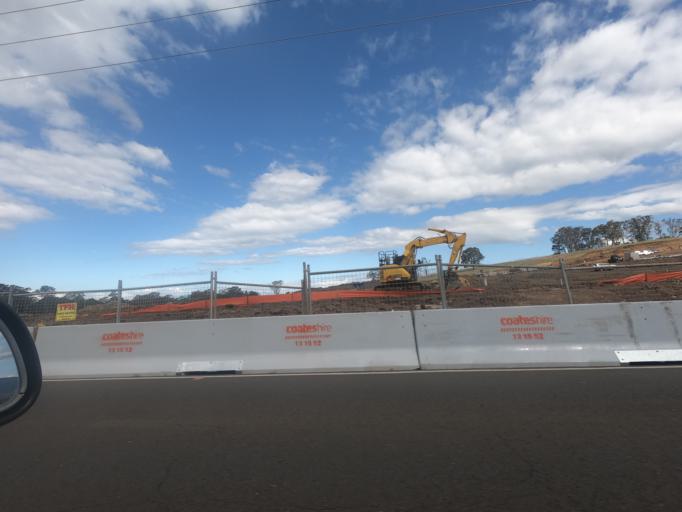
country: AU
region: New South Wales
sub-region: Wollongong
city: Dapto
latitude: -34.4759
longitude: 150.7882
